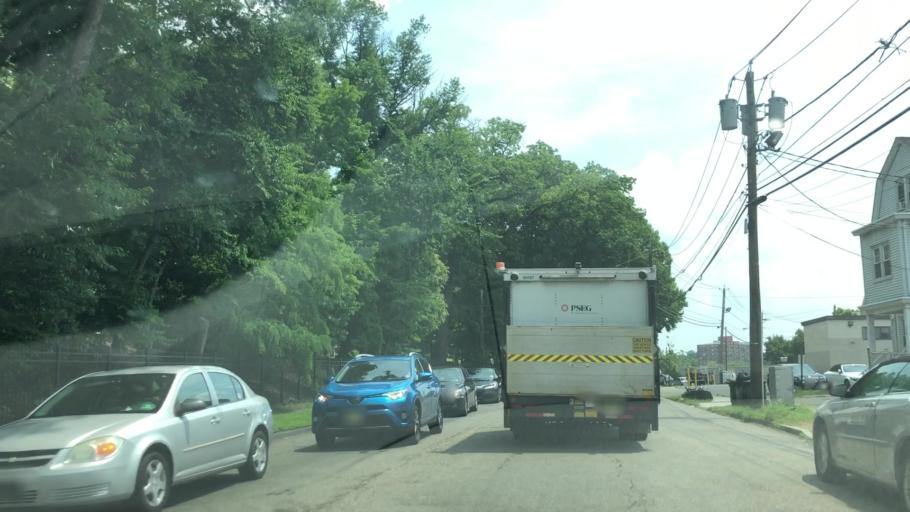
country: US
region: New Jersey
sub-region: Essex County
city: Orange
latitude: 40.7835
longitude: -74.2254
